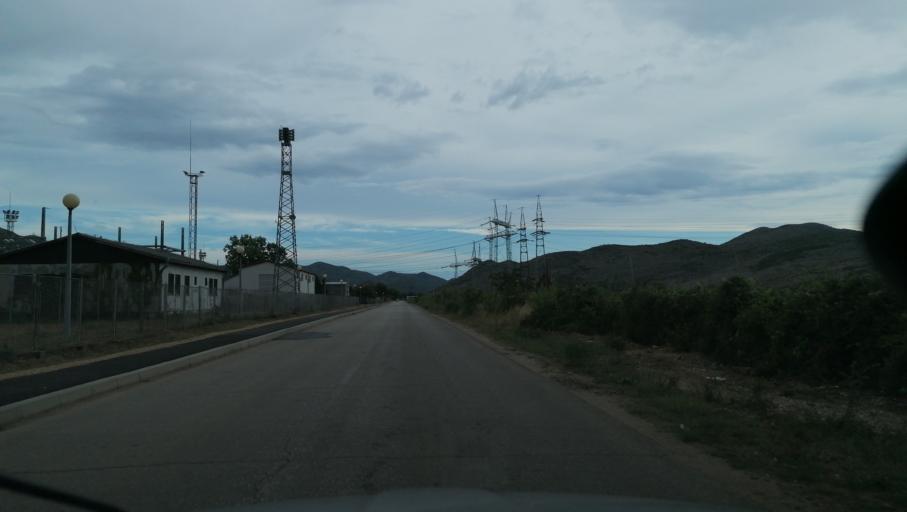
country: BA
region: Republika Srpska
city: Trebinje
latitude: 42.6787
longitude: 18.3325
